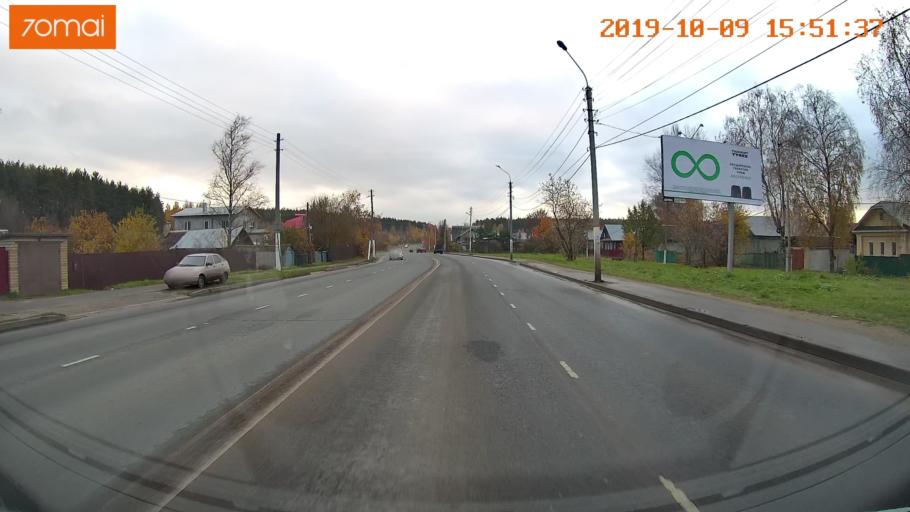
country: RU
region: Kostroma
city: Oktyabr'skiy
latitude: 57.7964
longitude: 40.9776
